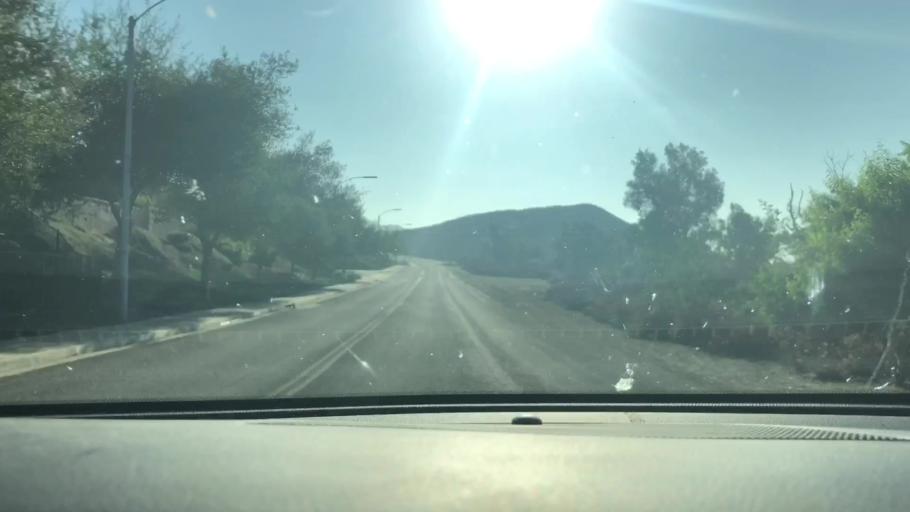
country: US
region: California
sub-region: Riverside County
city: Wildomar
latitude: 33.6051
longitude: -117.2365
